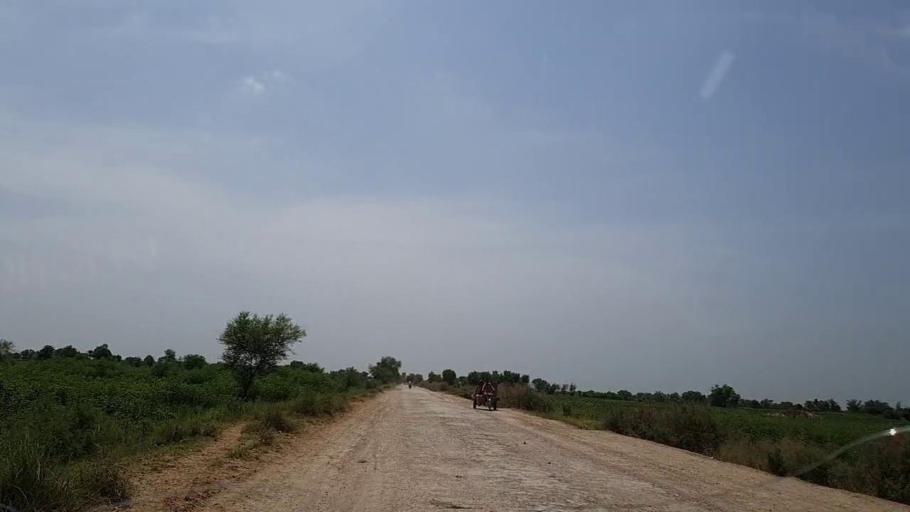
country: PK
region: Sindh
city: Khanpur
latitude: 27.8615
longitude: 69.4871
